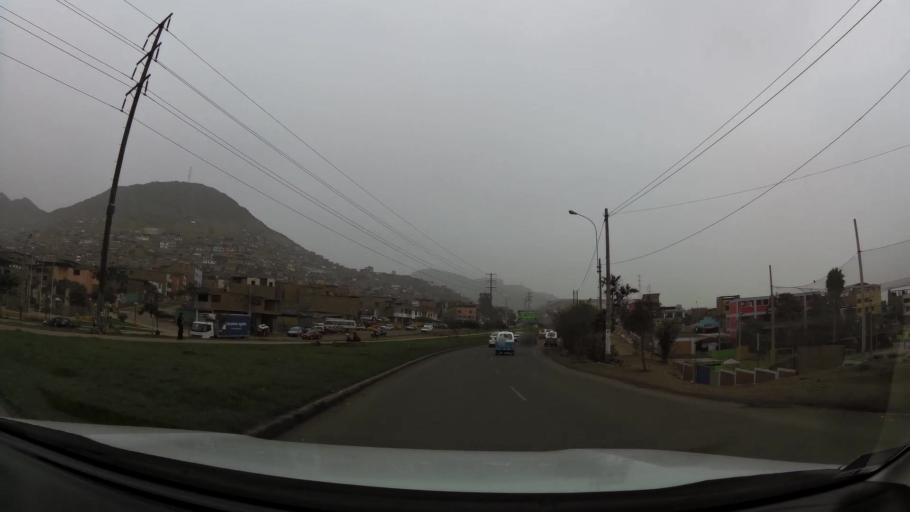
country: PE
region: Lima
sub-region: Lima
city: Surco
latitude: -12.1727
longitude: -76.9449
